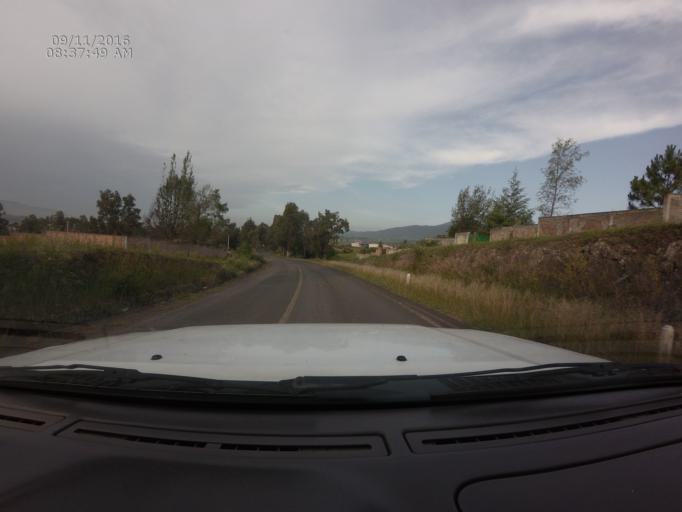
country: MX
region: Michoacan
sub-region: Morelia
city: La Mintzita (Piedra Dura)
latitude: 19.6232
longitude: -101.2760
